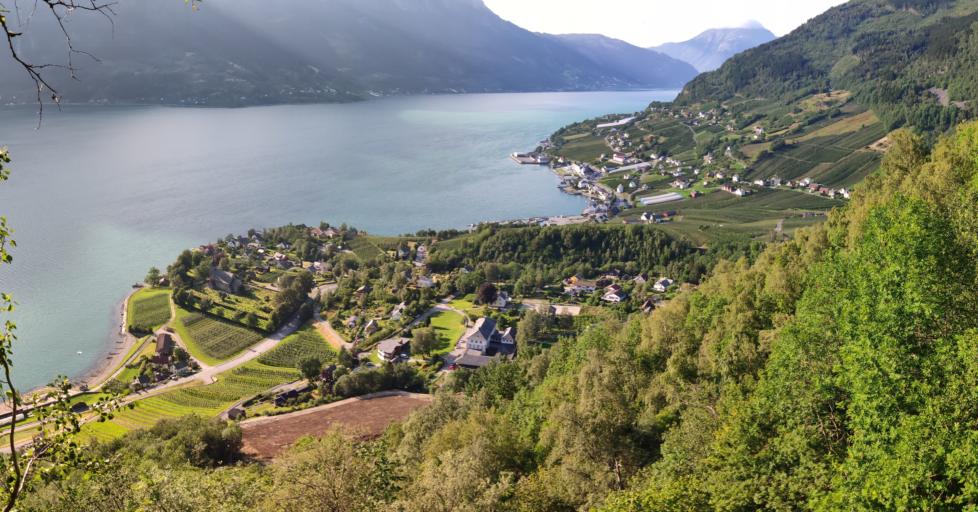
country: NO
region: Hordaland
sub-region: Ullensvang
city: Kinsarvik
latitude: 60.3148
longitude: 6.6607
